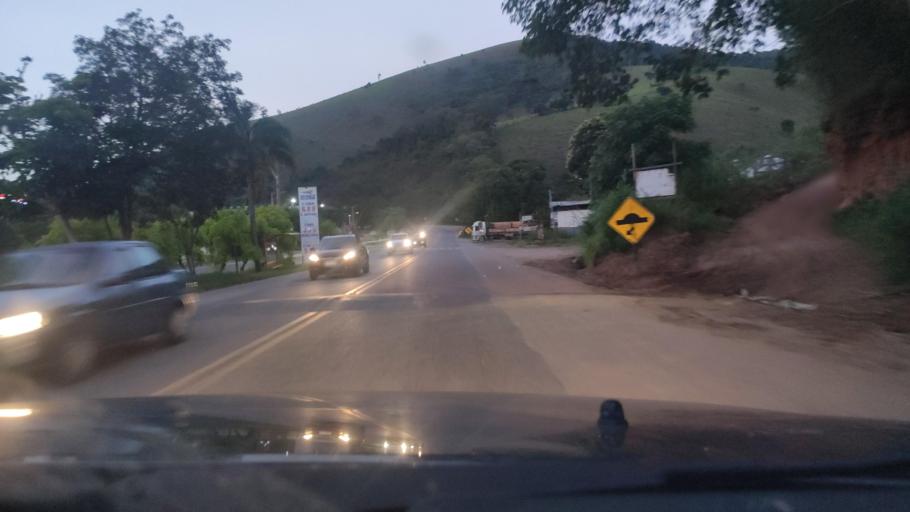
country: BR
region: Sao Paulo
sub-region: Campos Do Jordao
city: Campos do Jordao
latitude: -22.7443
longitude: -45.7396
